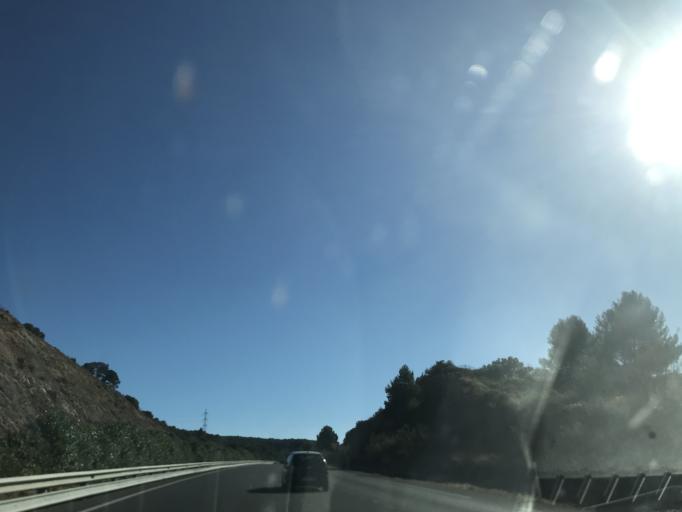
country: ES
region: Andalusia
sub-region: Provincia de Malaga
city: Antequera
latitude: 37.0369
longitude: -4.4855
